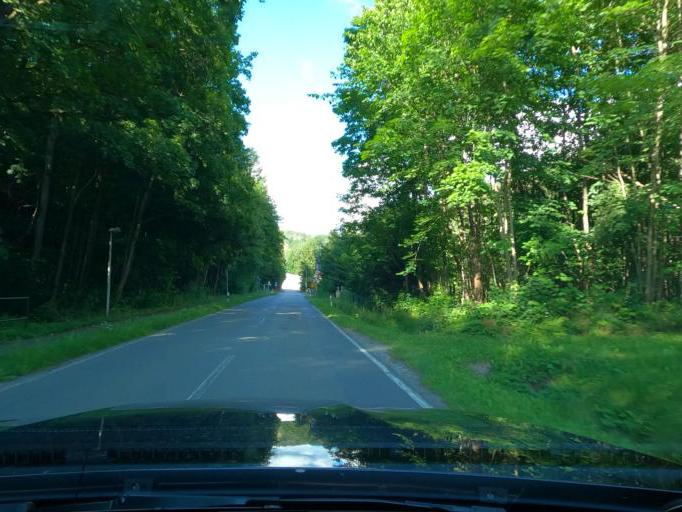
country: DE
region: Lower Saxony
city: Osterode am Harz
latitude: 51.7427
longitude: 10.2841
